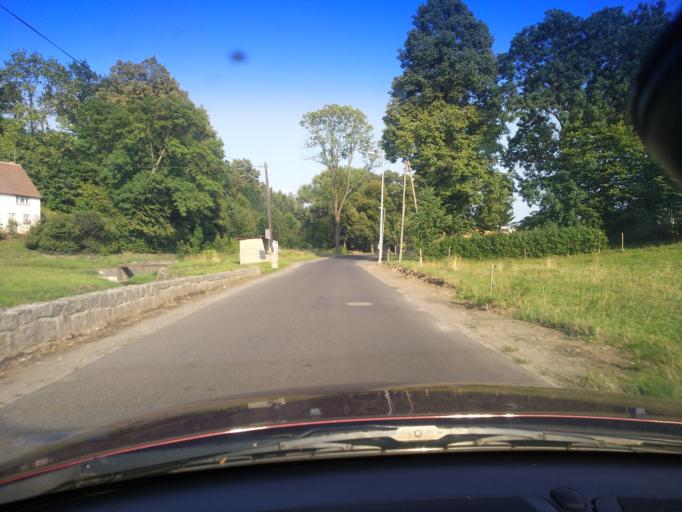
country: PL
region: Lower Silesian Voivodeship
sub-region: Powiat lubanski
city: Siekierczyn
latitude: 51.0679
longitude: 15.1661
